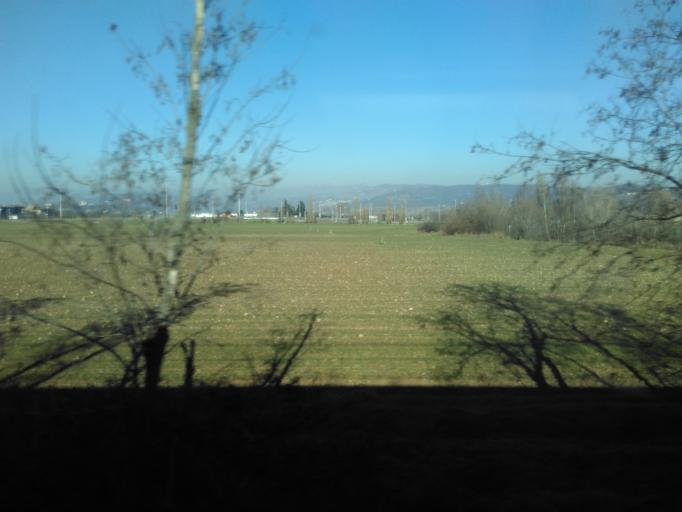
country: IT
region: Veneto
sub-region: Provincia di Verona
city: San Martino Buon Albergo
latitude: 45.4245
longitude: 11.0648
